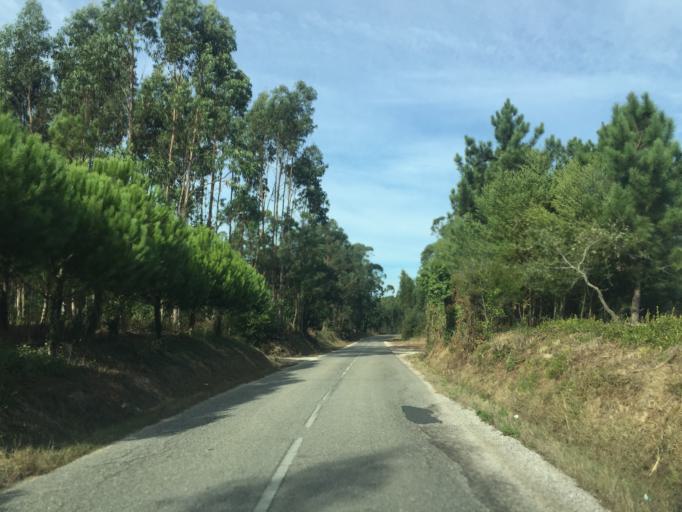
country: PT
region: Coimbra
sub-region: Figueira da Foz
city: Lavos
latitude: 40.0759
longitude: -8.8225
